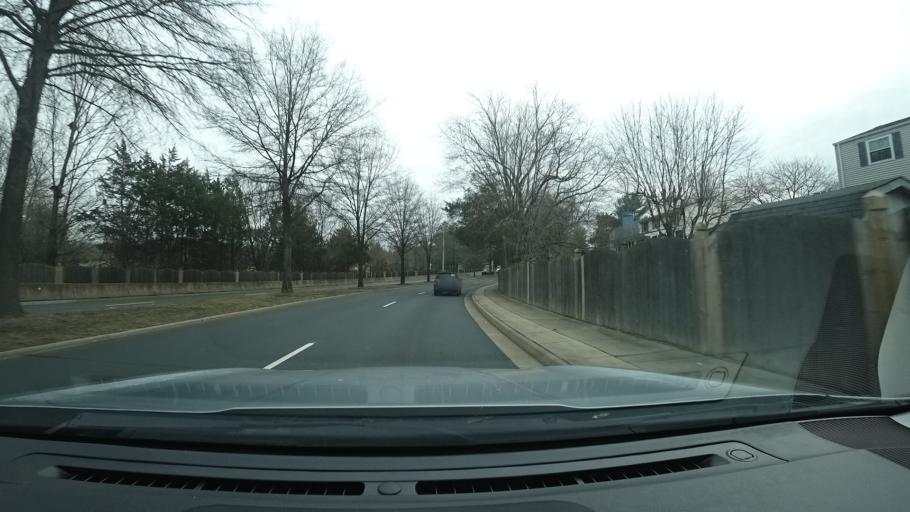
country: US
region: Virginia
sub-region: Fairfax County
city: Herndon
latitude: 38.9801
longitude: -77.3708
